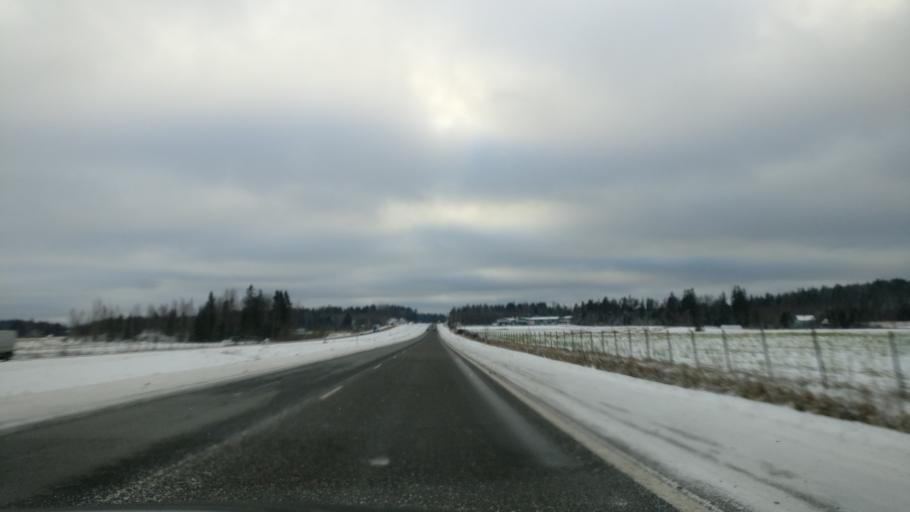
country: FI
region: Paijanne Tavastia
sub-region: Lahti
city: Lahti
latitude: 60.9109
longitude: 25.6170
